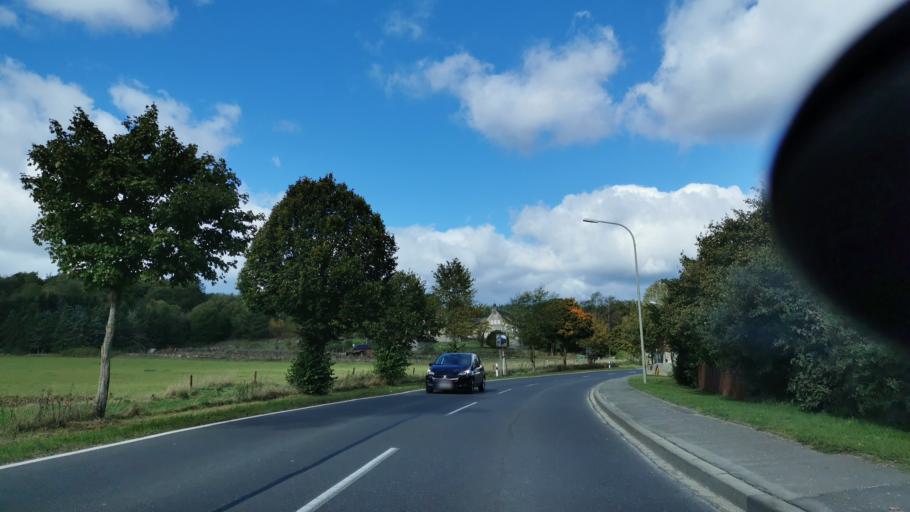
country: DE
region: Rheinland-Pfalz
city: Berndorf
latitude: 50.3148
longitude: 6.7249
